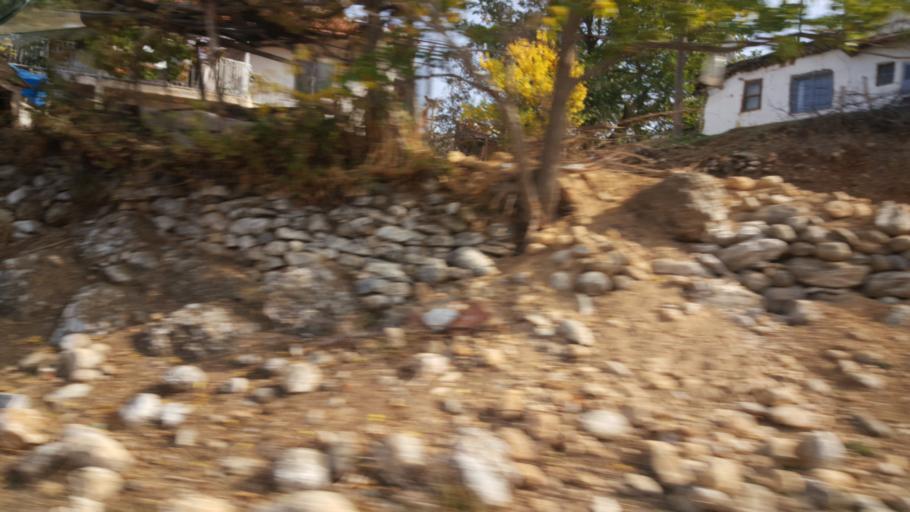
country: TR
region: Eskisehir
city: Mihaliccik
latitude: 39.9771
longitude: 31.3716
